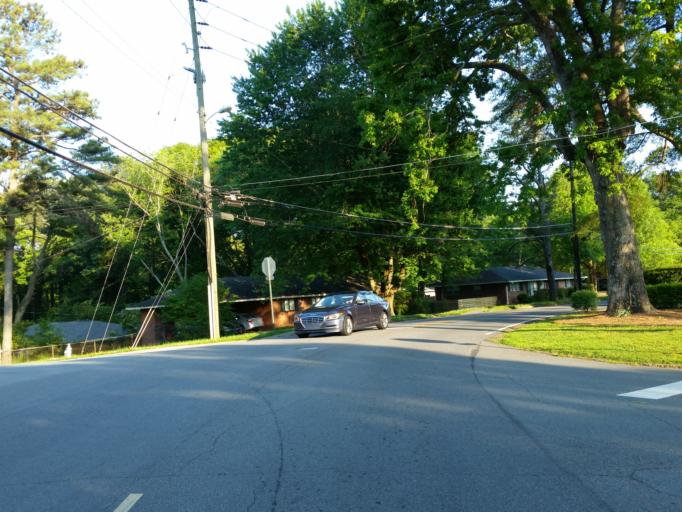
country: US
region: Georgia
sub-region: Cobb County
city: Smyrna
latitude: 33.9396
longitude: -84.4813
